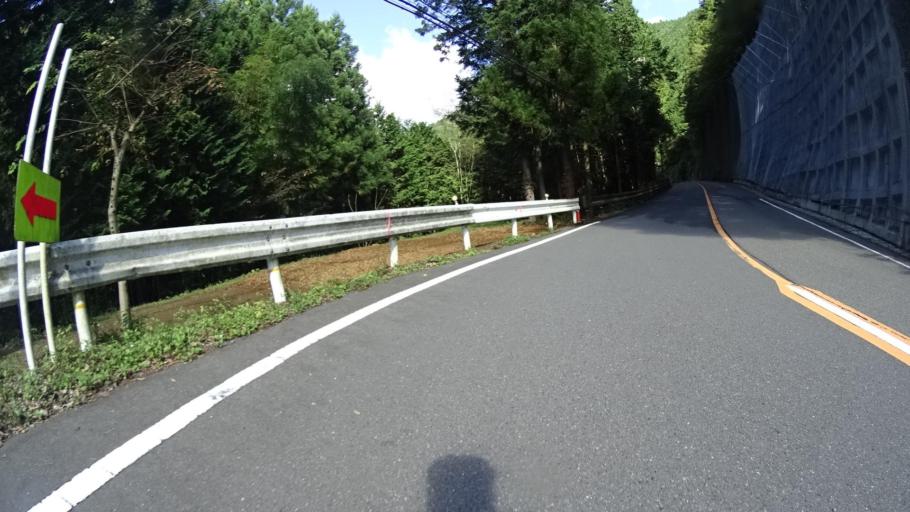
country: JP
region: Yamanashi
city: Uenohara
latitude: 35.7371
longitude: 139.0899
